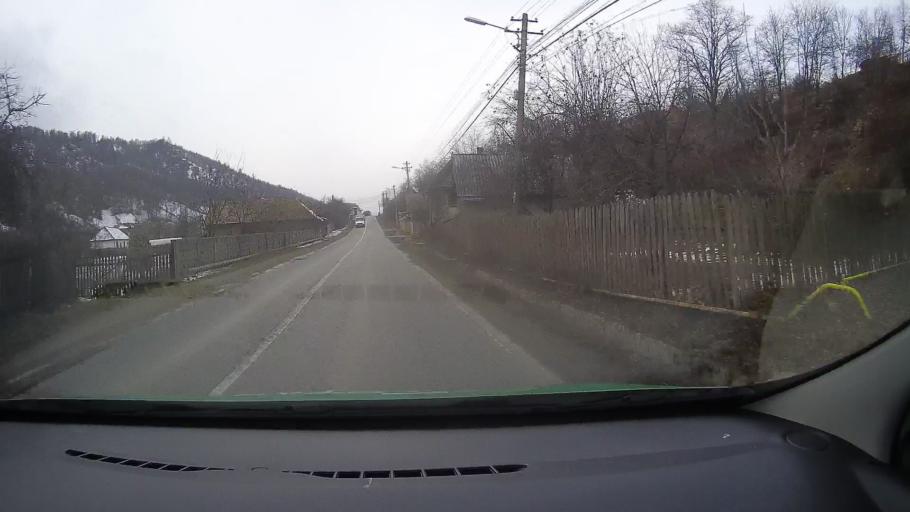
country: RO
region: Alba
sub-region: Oras Zlatna
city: Zlatna
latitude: 46.0918
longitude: 23.2583
